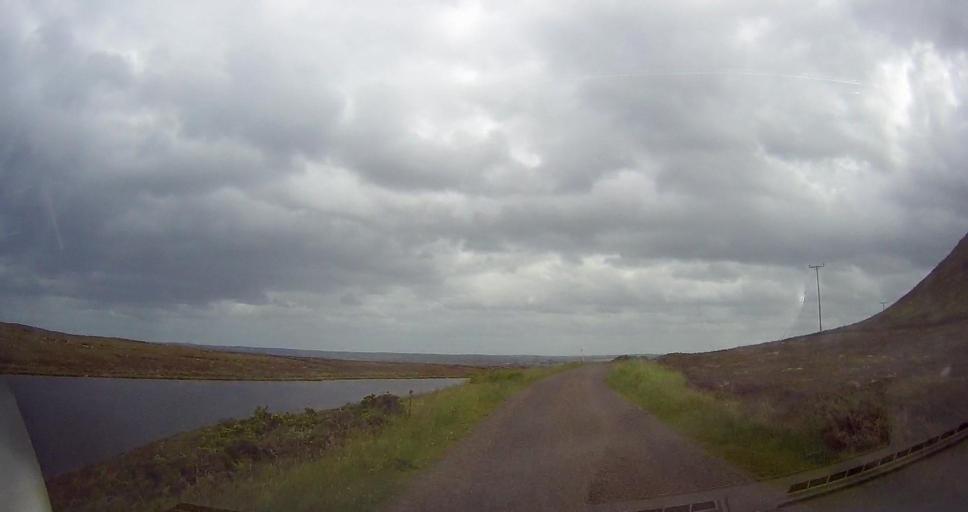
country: GB
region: Scotland
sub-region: Highland
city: Thurso
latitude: 58.6619
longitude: -3.3723
